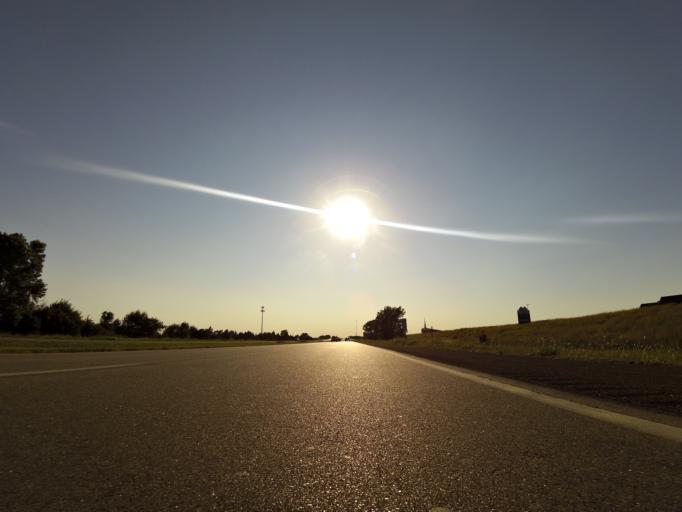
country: US
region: Kansas
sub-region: Sedgwick County
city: Maize
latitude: 37.7599
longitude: -97.4166
